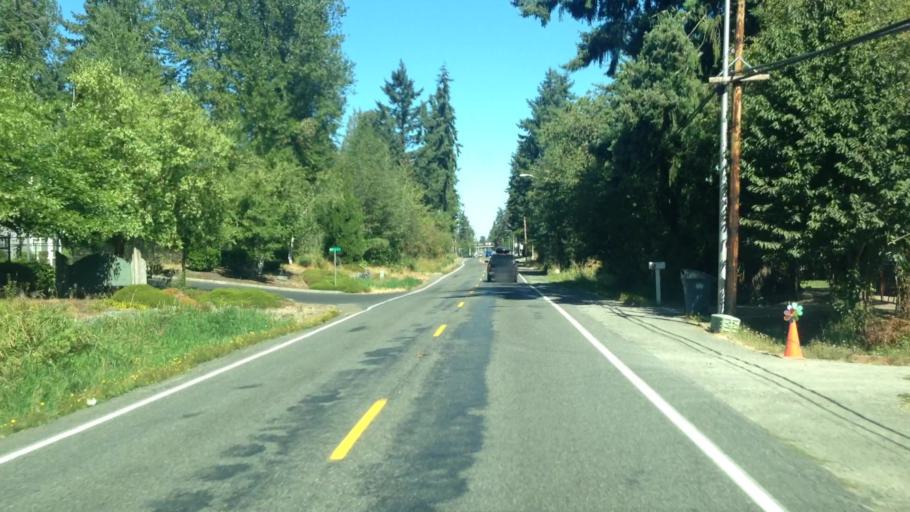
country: US
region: Washington
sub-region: Pierce County
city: Midland
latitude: 47.1517
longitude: -122.4155
